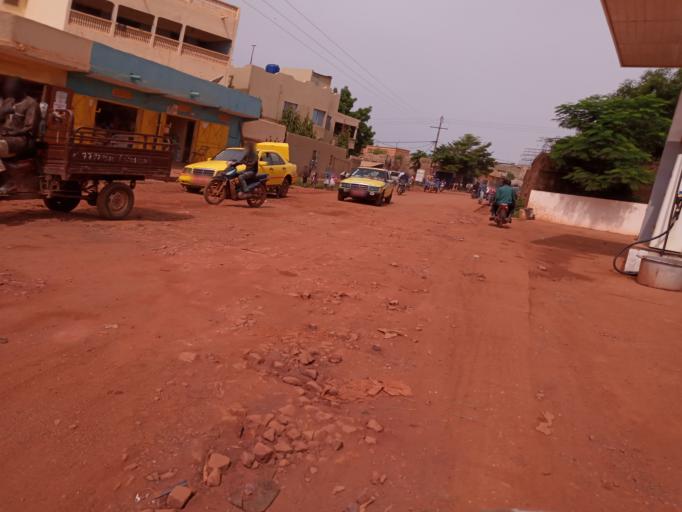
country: ML
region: Bamako
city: Bamako
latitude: 12.5539
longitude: -7.9921
